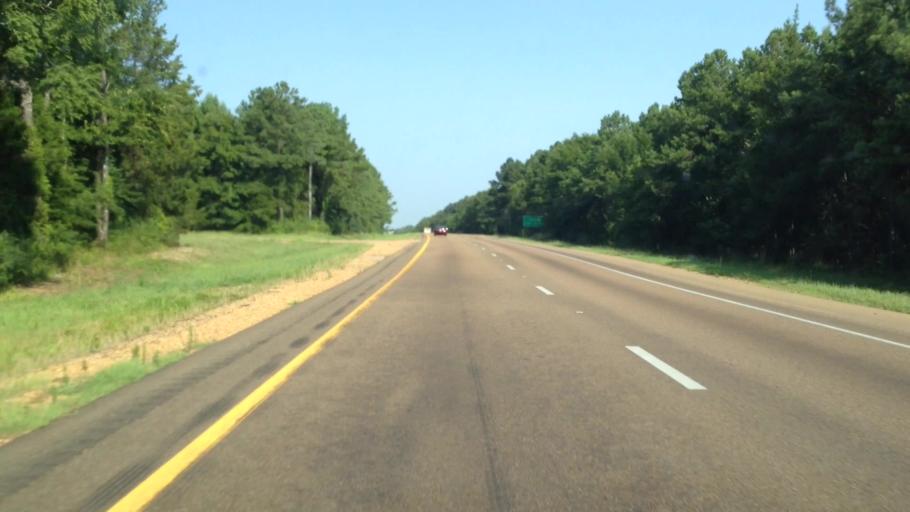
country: US
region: Mississippi
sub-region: Hinds County
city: Clinton
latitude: 32.3112
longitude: -90.2974
